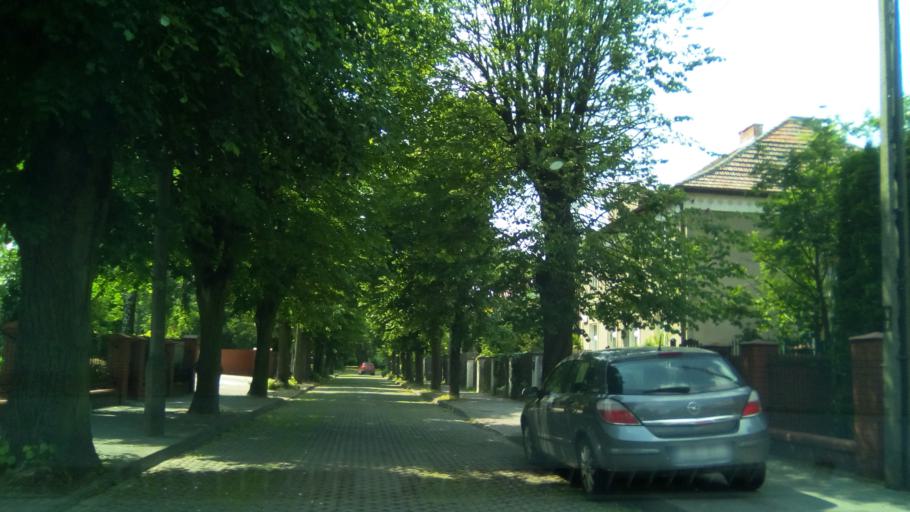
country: PL
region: Greater Poland Voivodeship
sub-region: Powiat gnieznienski
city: Gniezno
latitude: 52.5341
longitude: 17.6156
